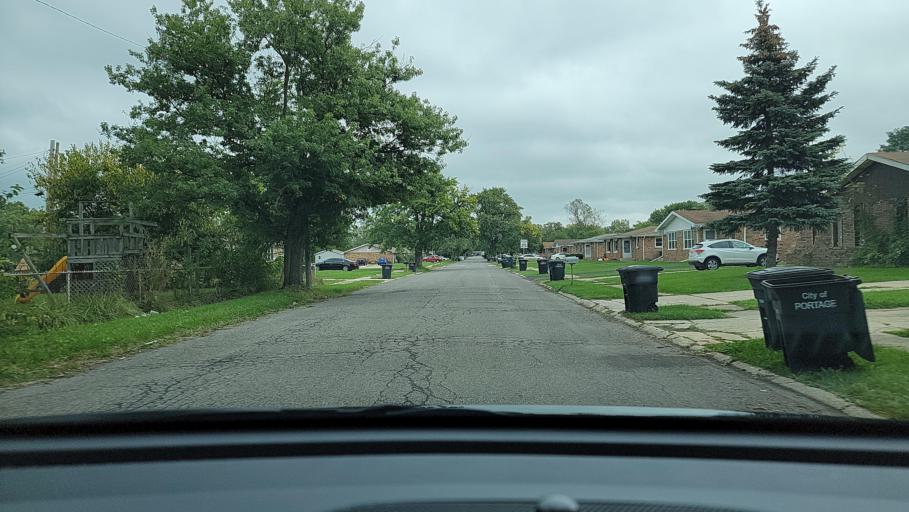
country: US
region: Indiana
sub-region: Porter County
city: Portage
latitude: 41.5556
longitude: -87.2034
